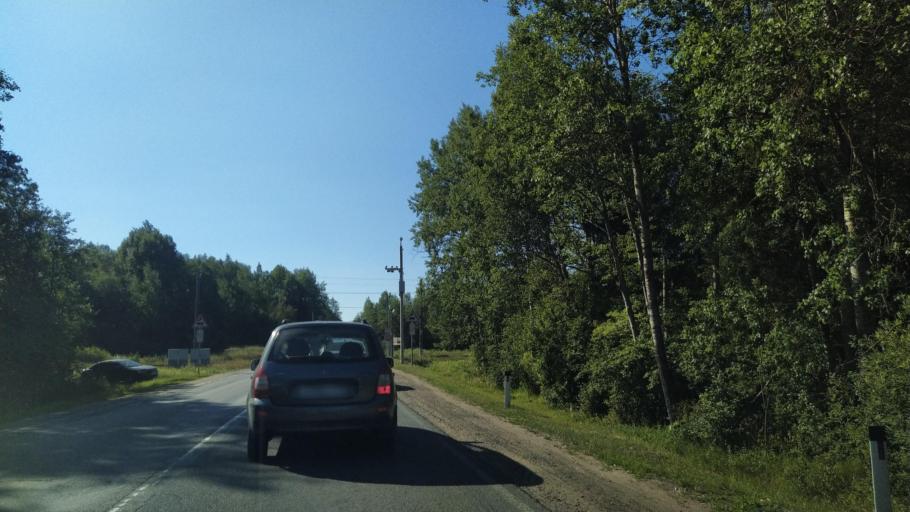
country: RU
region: Leningrad
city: Kirovsk
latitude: 59.9260
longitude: 30.9658
